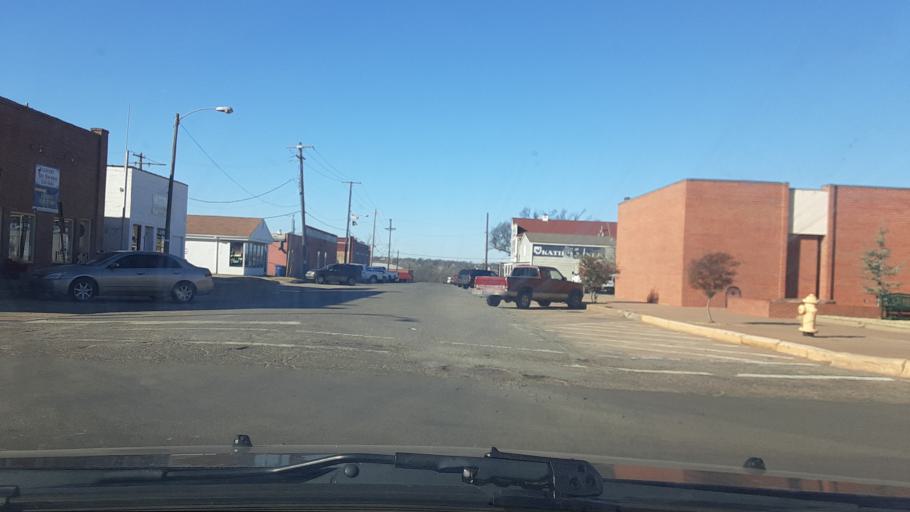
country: US
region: Oklahoma
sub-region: Logan County
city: Guthrie
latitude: 35.8791
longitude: -97.4254
